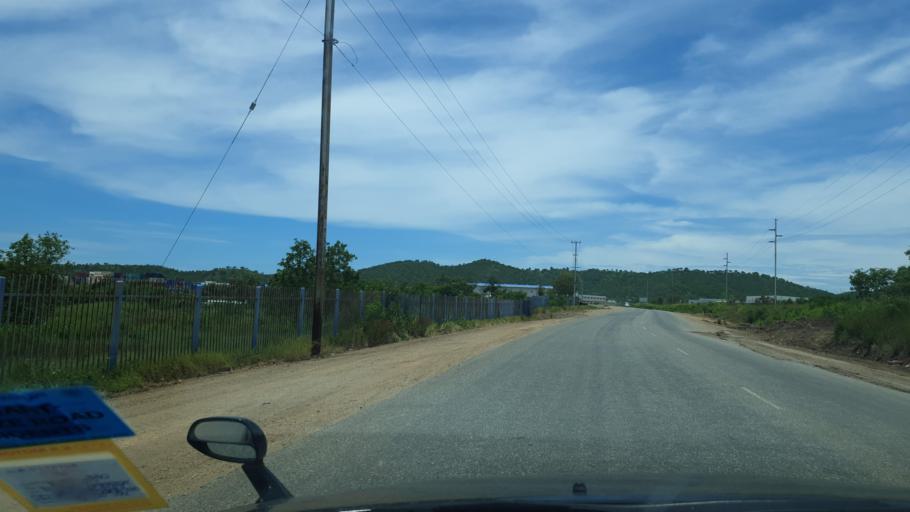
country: PG
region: National Capital
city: Port Moresby
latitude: -9.4195
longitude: 147.0863
